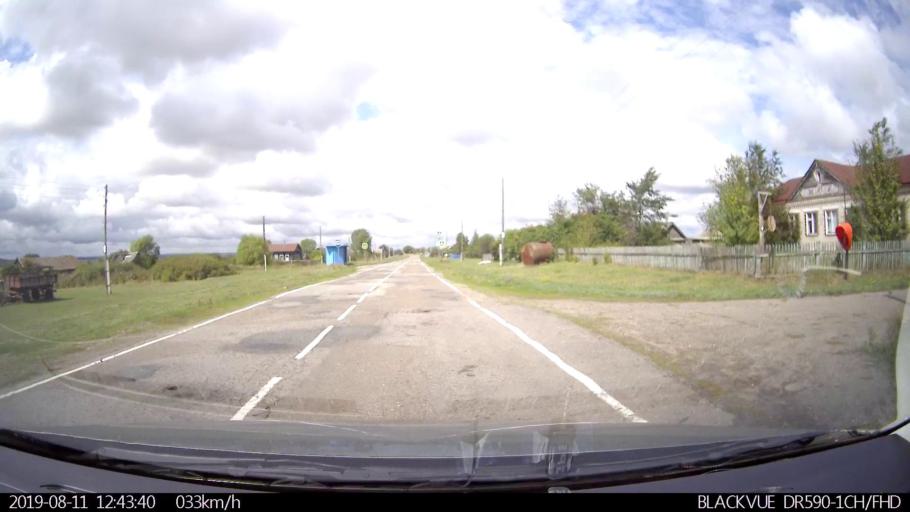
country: RU
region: Ulyanovsk
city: Ignatovka
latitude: 53.8516
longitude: 47.7415
